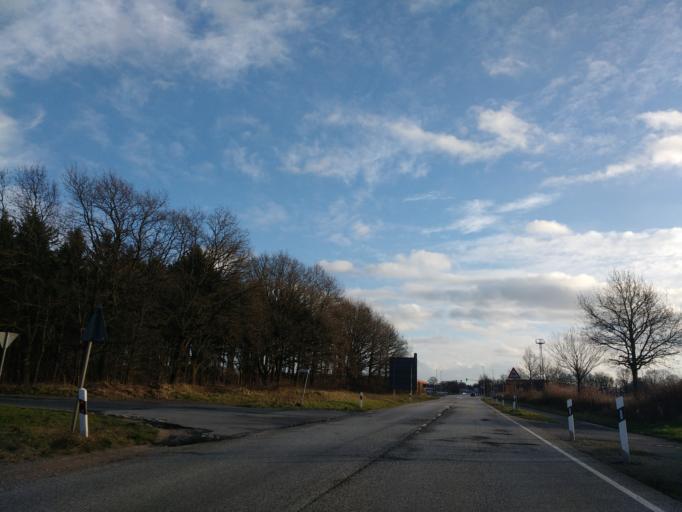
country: DE
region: Schleswig-Holstein
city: Kaltenkirchen
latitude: 53.8460
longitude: 9.9395
